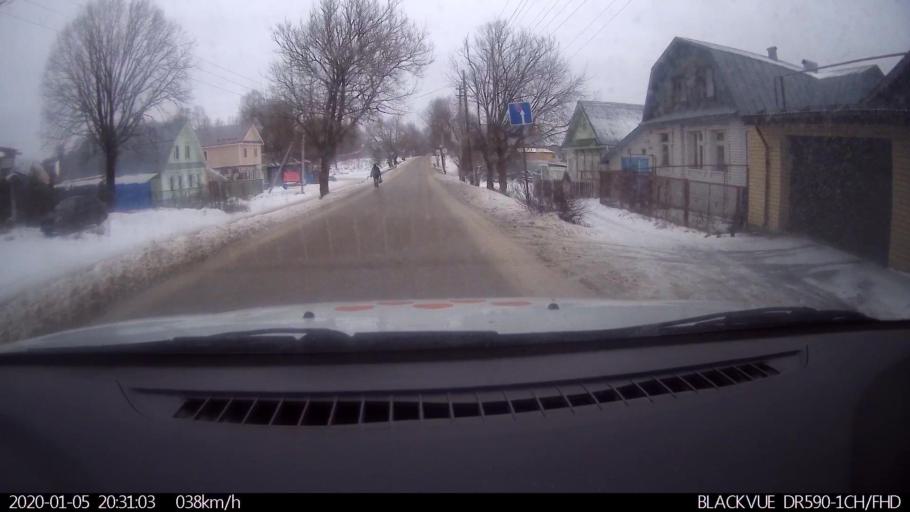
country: RU
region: Nizjnij Novgorod
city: Lukino
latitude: 56.4031
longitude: 43.7291
